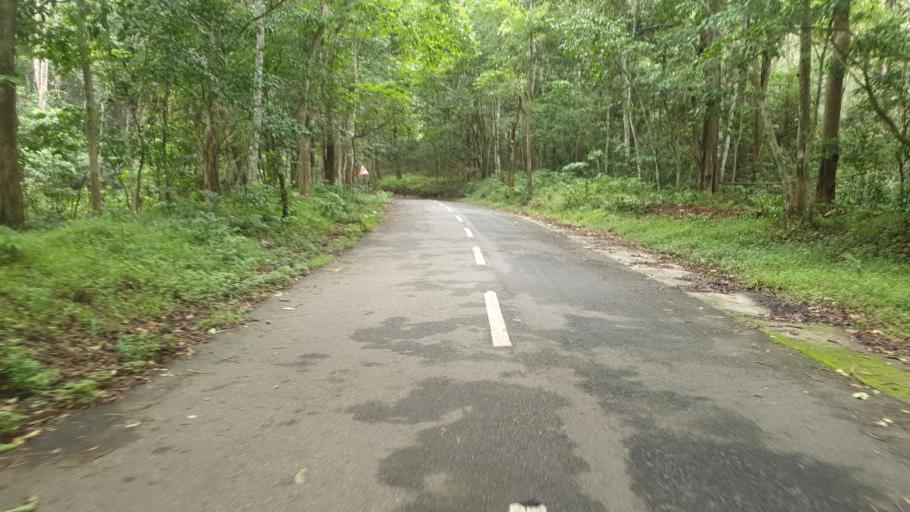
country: IN
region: Kerala
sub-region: Thiruvananthapuram
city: Nedumangad
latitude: 8.6472
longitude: 77.1075
